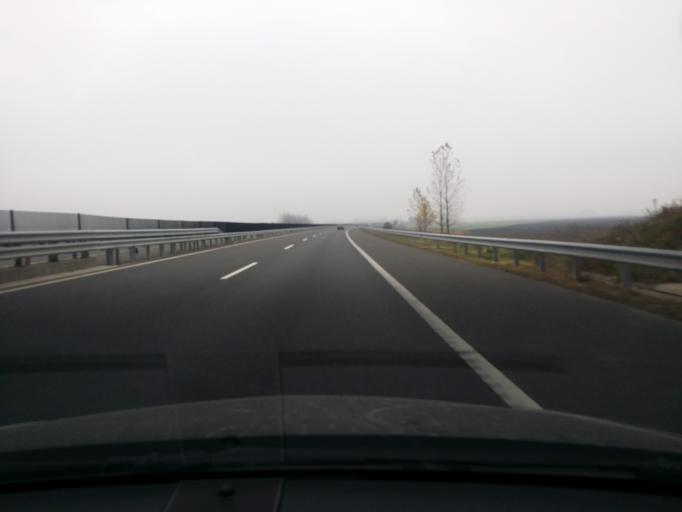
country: HU
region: Hajdu-Bihar
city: Hajdunanas
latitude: 47.8997
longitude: 21.4812
